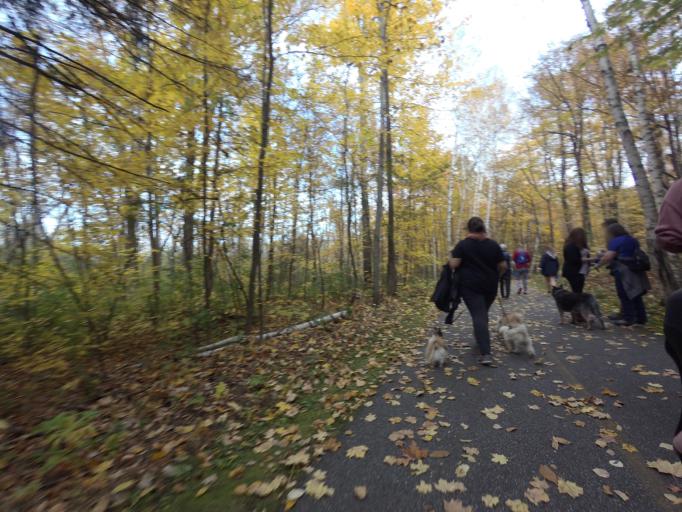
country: CA
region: Quebec
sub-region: Outaouais
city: Gatineau
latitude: 45.4475
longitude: -75.7637
